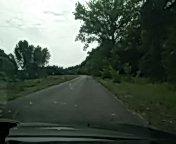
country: HU
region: Hajdu-Bihar
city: Debrecen
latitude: 47.4993
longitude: 21.7328
